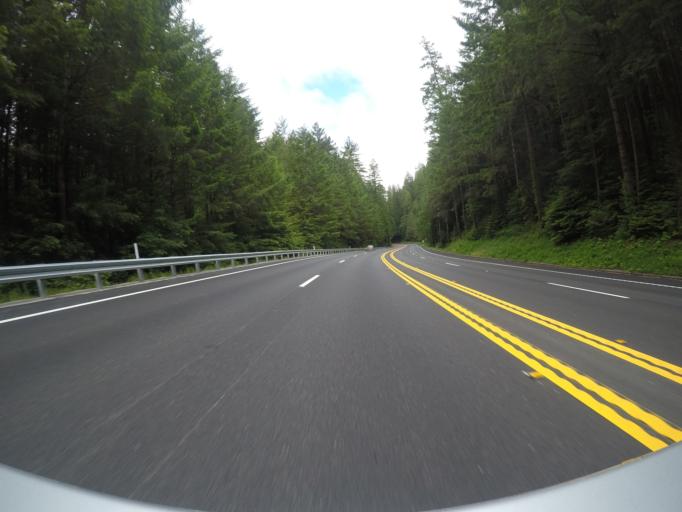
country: US
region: California
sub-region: Humboldt County
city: Rio Dell
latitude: 40.3404
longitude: -123.9339
